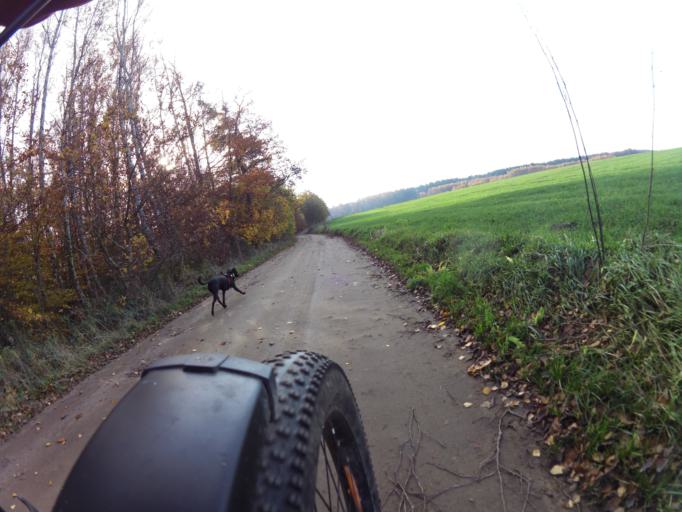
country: PL
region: Pomeranian Voivodeship
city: Strzelno
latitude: 54.7461
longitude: 18.2867
